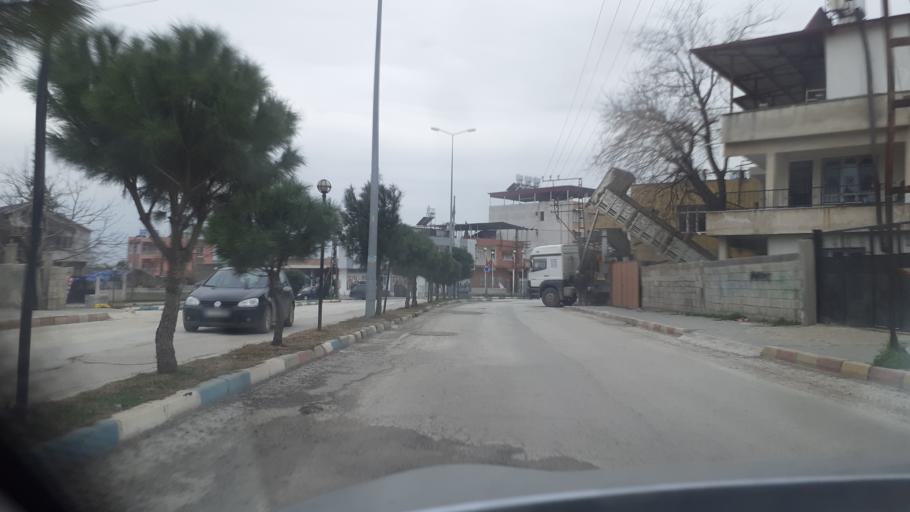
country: TR
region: Hatay
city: Kirikhan
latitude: 36.4918
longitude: 36.3574
